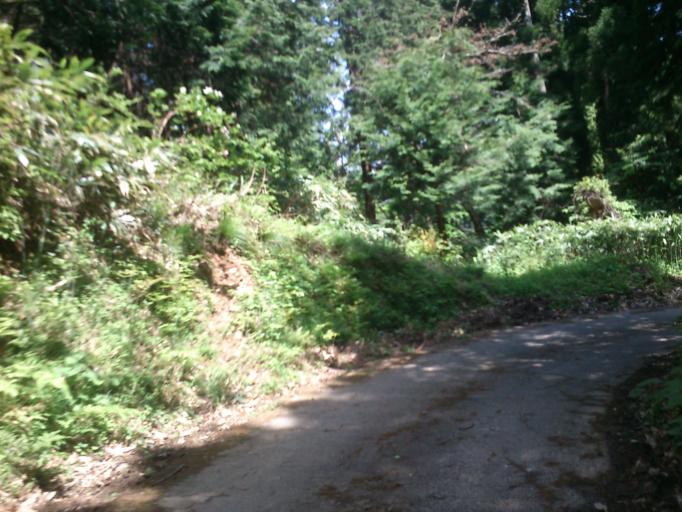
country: JP
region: Kyoto
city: Miyazu
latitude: 35.6077
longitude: 135.1958
